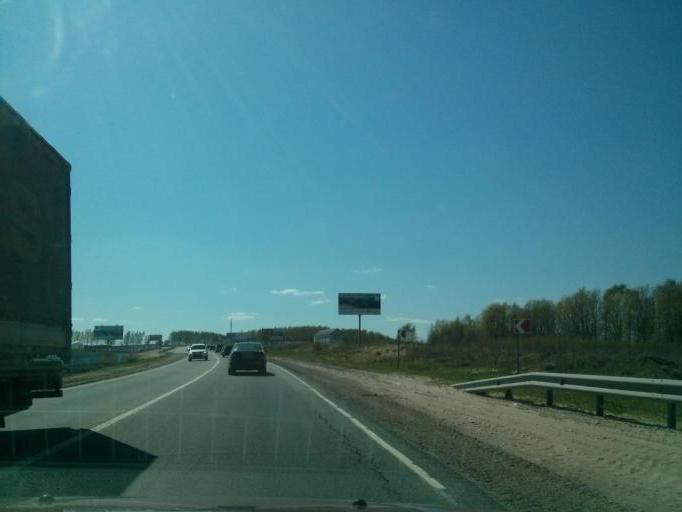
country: RU
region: Nizjnij Novgorod
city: Burevestnik
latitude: 56.2001
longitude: 43.8515
